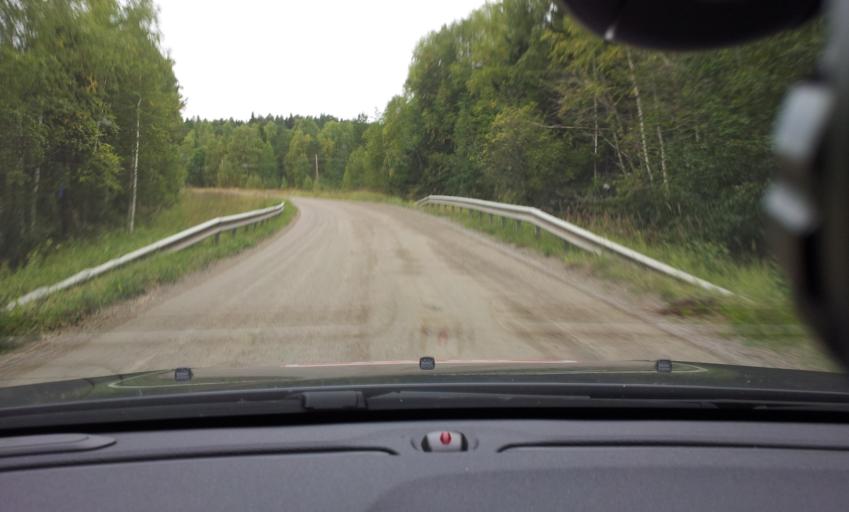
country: SE
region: Jaemtland
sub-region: OEstersunds Kommun
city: Brunflo
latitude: 62.9622
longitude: 15.0184
